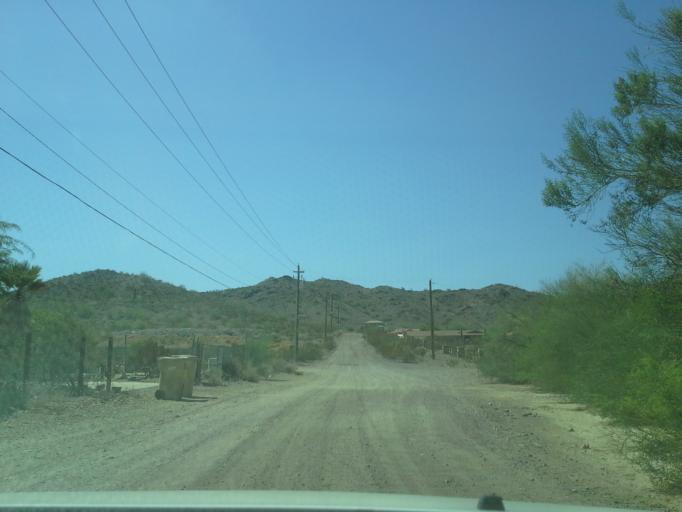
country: US
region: Arizona
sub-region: Maricopa County
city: Laveen
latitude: 33.3526
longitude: -112.1519
